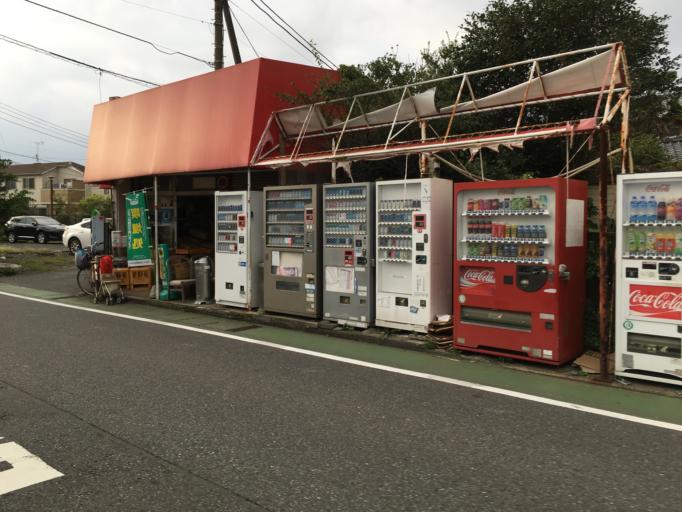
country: JP
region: Chiba
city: Kashiwa
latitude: 35.8034
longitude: 139.9588
